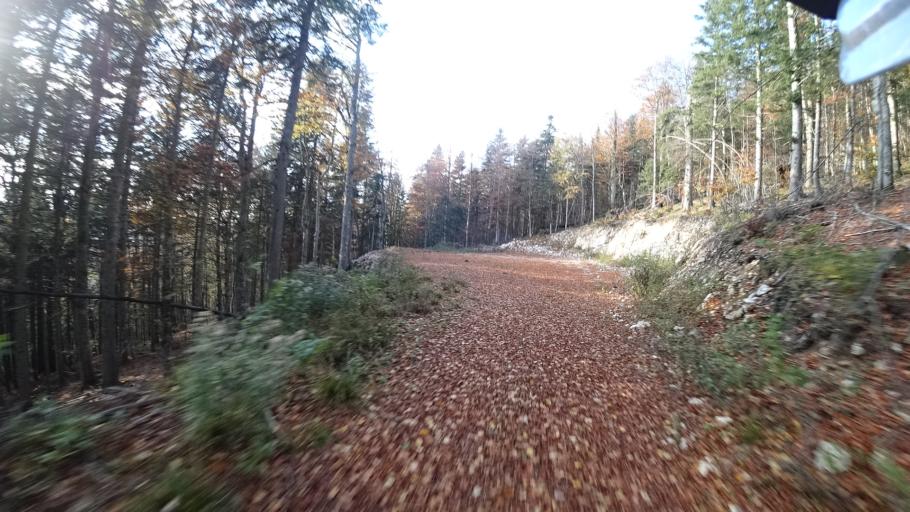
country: HR
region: Karlovacka
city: Plaski
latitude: 44.9559
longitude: 15.3970
